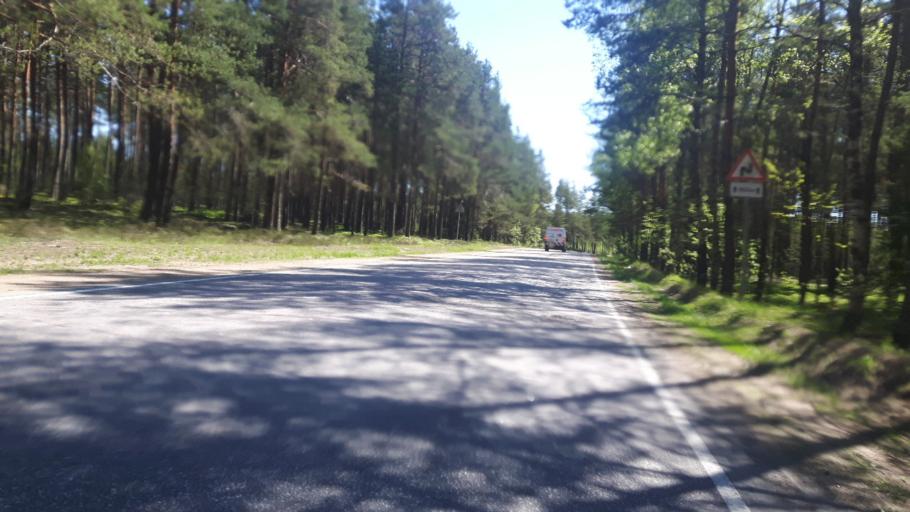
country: RU
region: Leningrad
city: Glebychevo
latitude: 60.3464
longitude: 28.8209
